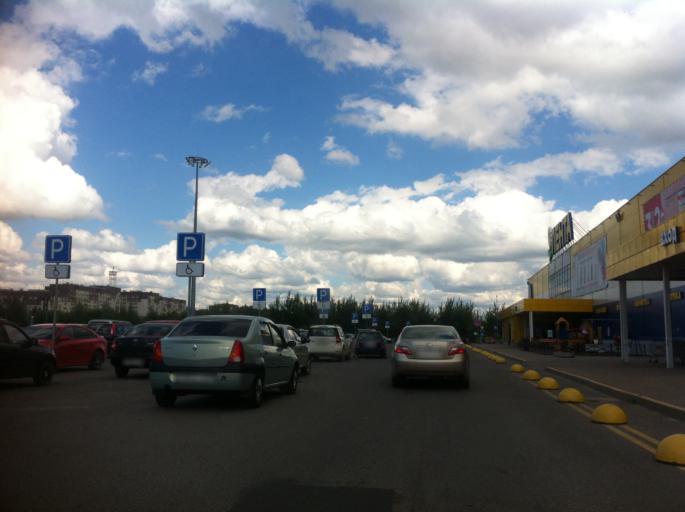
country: RU
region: Pskov
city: Pskov
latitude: 57.8052
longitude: 28.2671
